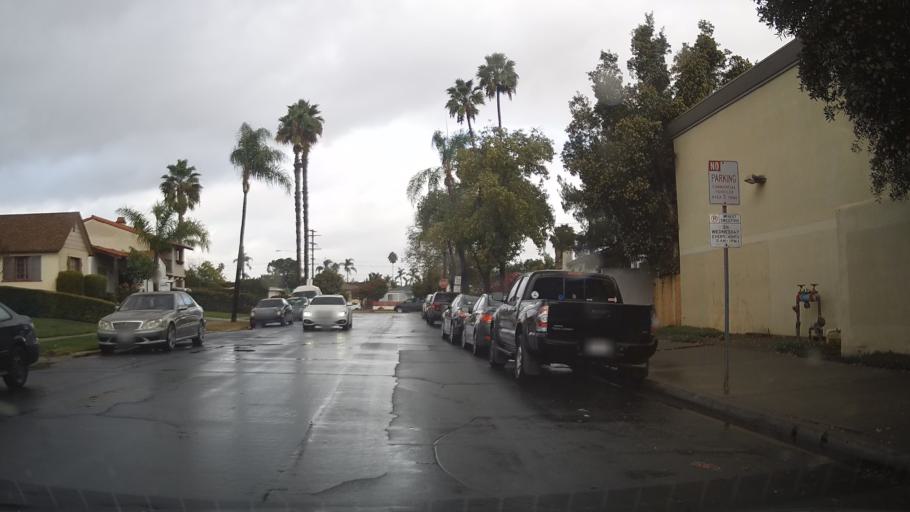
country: US
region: California
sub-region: San Diego County
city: San Diego
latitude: 32.7644
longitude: -117.1150
